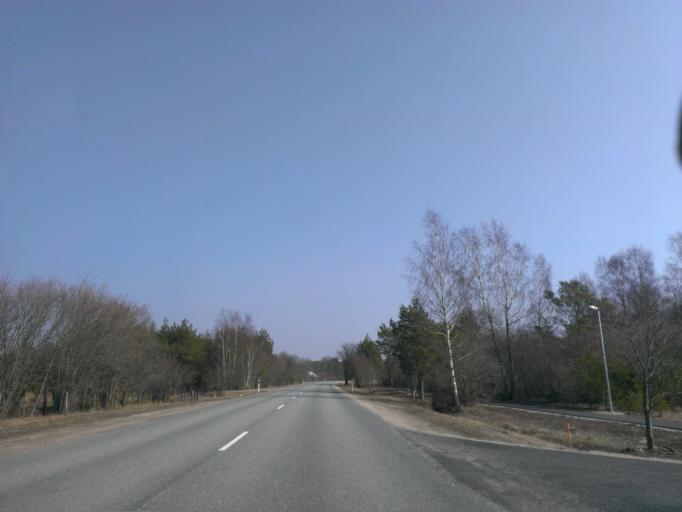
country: EE
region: Saare
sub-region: Kuressaare linn
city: Kuressaare
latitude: 58.2628
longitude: 22.5792
